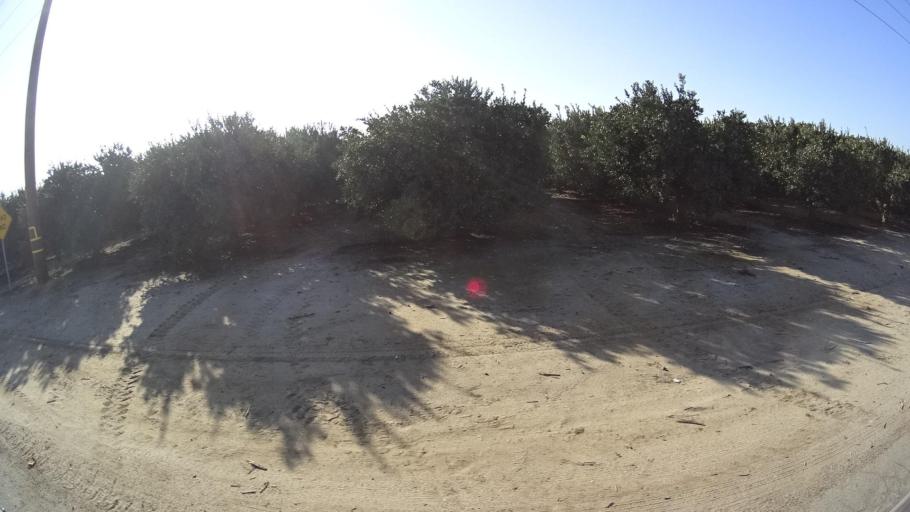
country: US
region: California
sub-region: Tulare County
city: Richgrove
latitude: 35.7326
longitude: -119.1333
